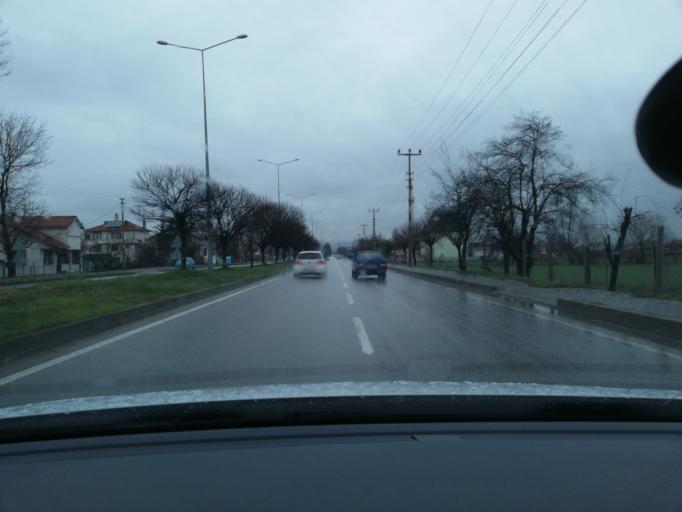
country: TR
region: Bolu
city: Bolu
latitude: 40.7053
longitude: 31.6176
